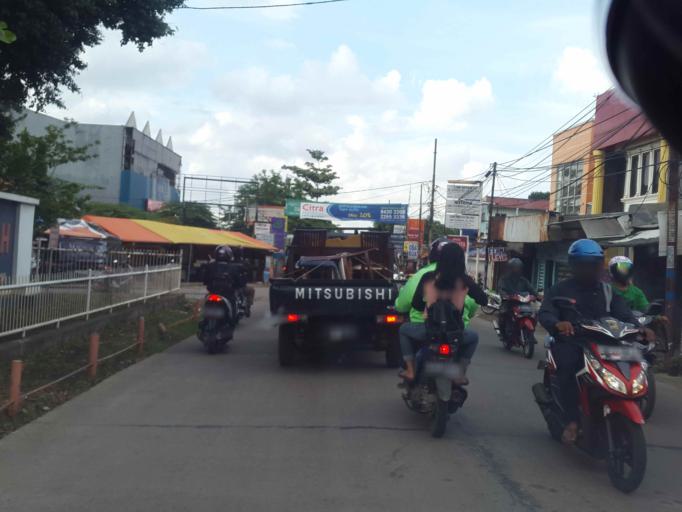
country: ID
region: West Java
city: Bekasi
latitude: -6.2921
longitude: 106.9181
